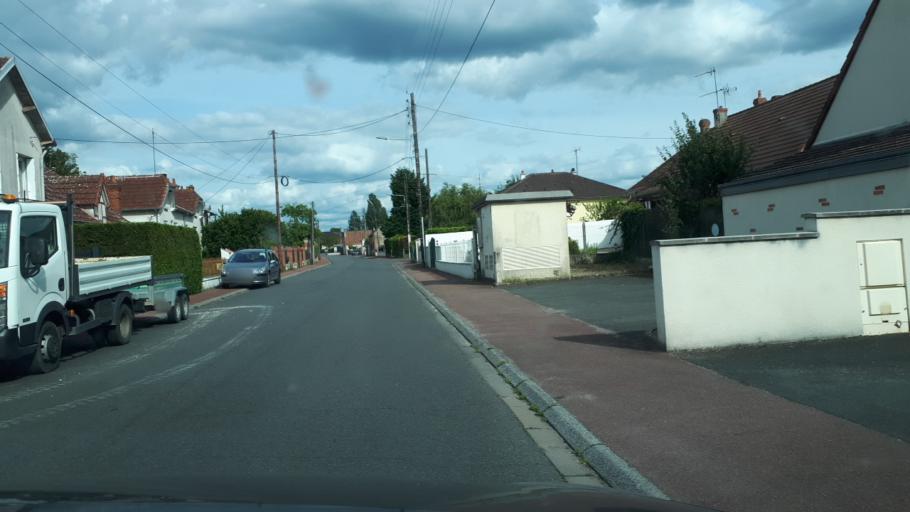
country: FR
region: Centre
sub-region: Departement du Loir-et-Cher
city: Romorantin-Lanthenay
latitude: 47.3524
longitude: 1.7544
